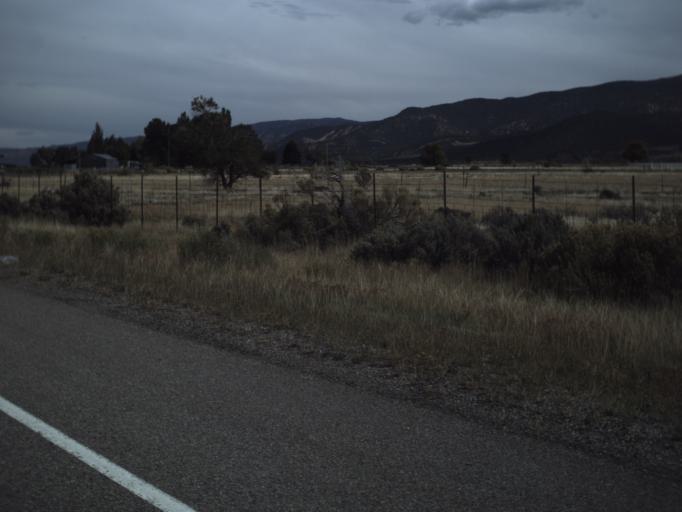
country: US
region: Utah
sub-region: Iron County
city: Enoch
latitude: 37.8041
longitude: -112.9435
